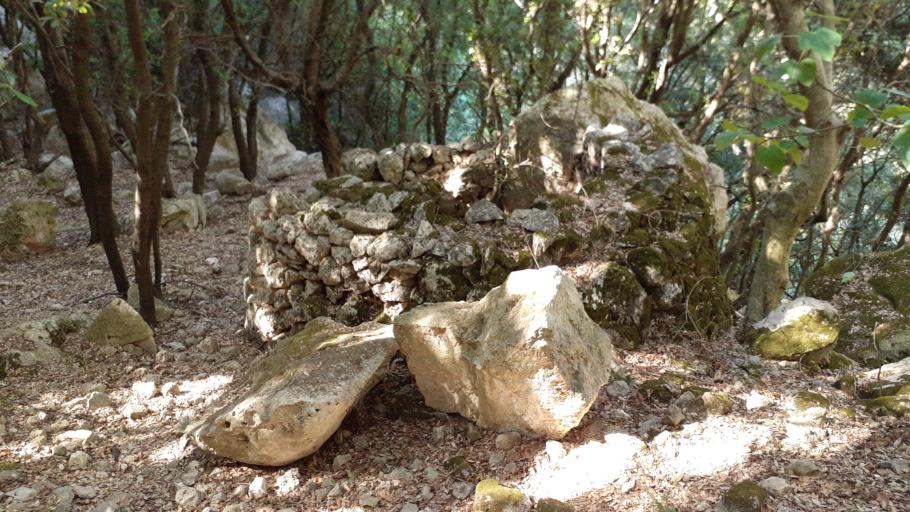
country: IT
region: Sicily
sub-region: Provincia di Siracusa
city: Canicattini Bagni
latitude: 36.9727
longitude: 15.0849
